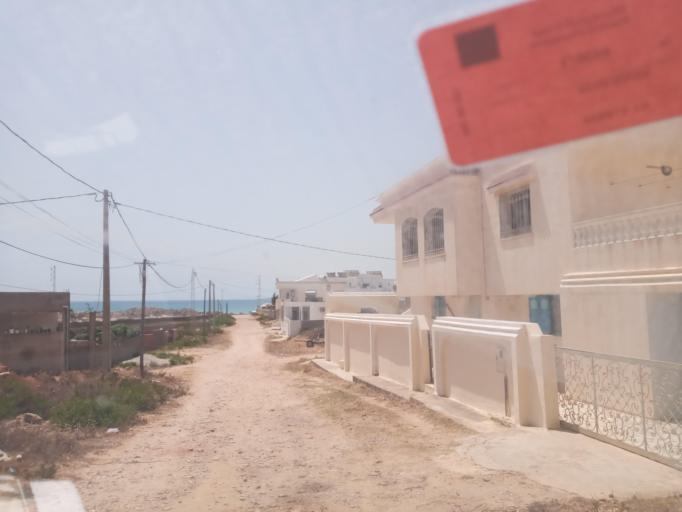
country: TN
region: Nabul
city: El Haouaria
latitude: 37.0427
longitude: 11.0615
